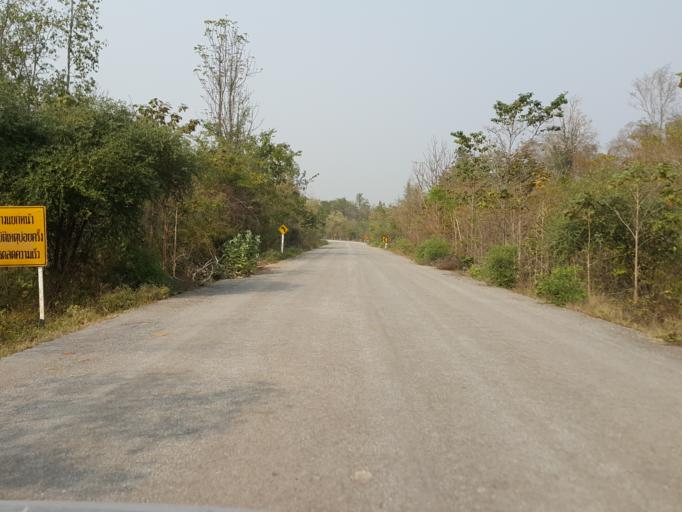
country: TH
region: Lampang
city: Mae Phrik
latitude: 17.5015
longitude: 99.0832
